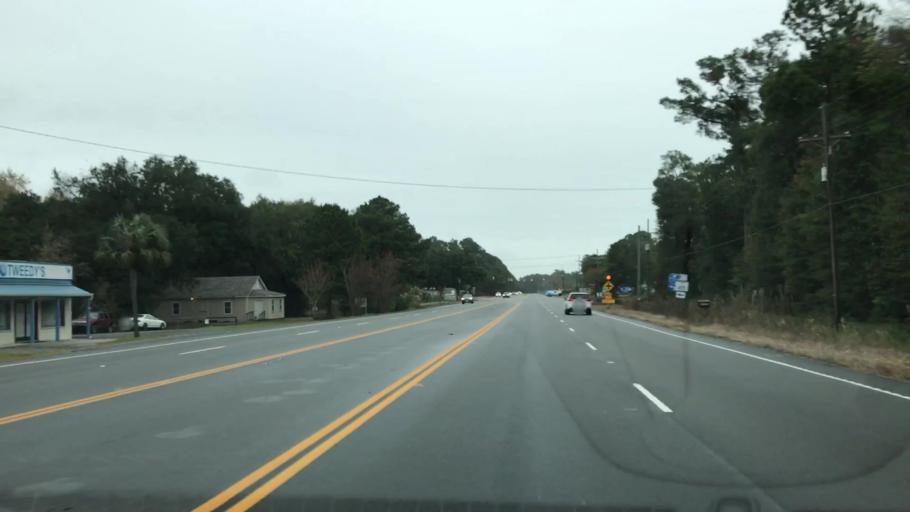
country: US
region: South Carolina
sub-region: Charleston County
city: Awendaw
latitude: 33.0939
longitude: -79.4783
